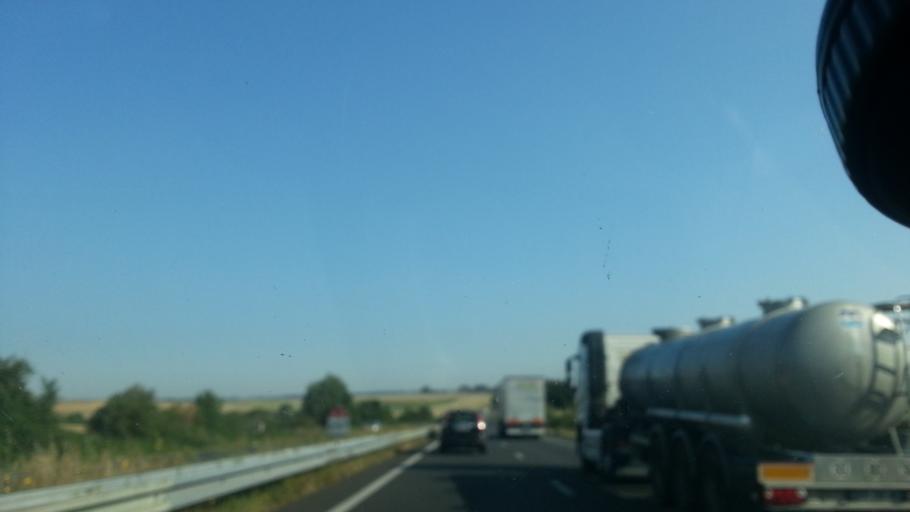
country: FR
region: Poitou-Charentes
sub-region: Departement de la Vienne
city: Les Ormes
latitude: 46.9698
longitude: 0.5474
